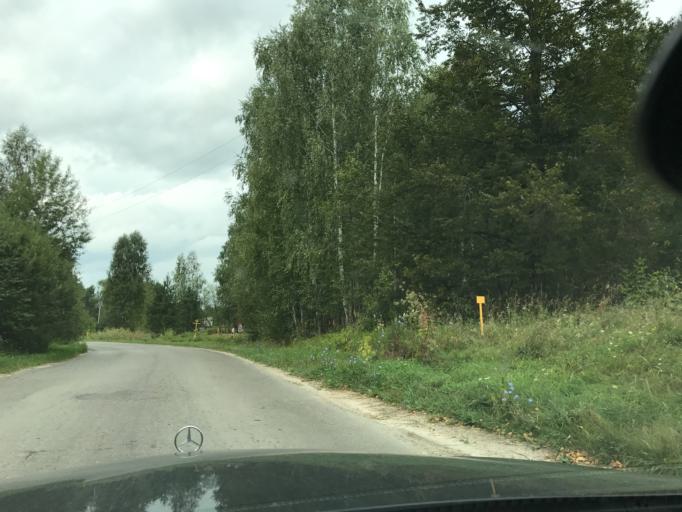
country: RU
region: Vladimir
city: Galitsy
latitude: 55.9943
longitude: 42.8197
